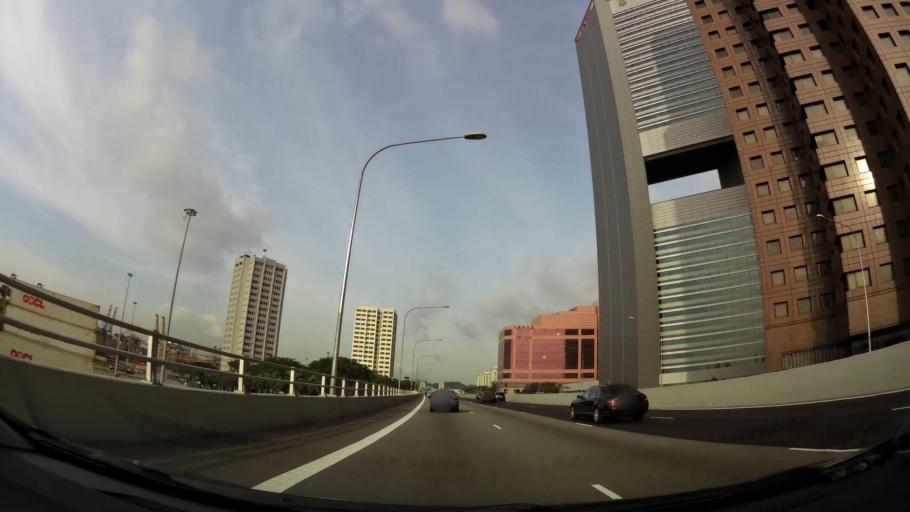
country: SG
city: Singapore
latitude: 1.2726
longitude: 103.8447
